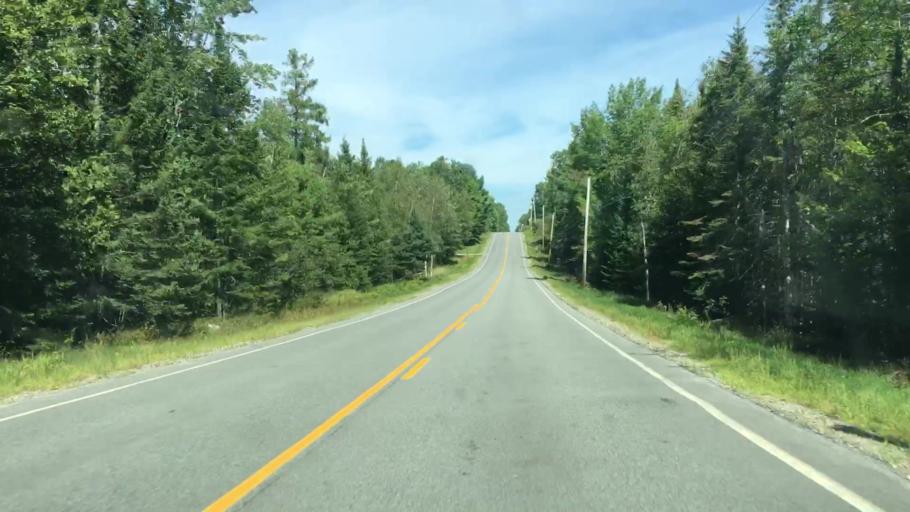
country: US
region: Maine
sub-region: Penobscot County
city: Howland
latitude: 45.2099
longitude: -68.8016
